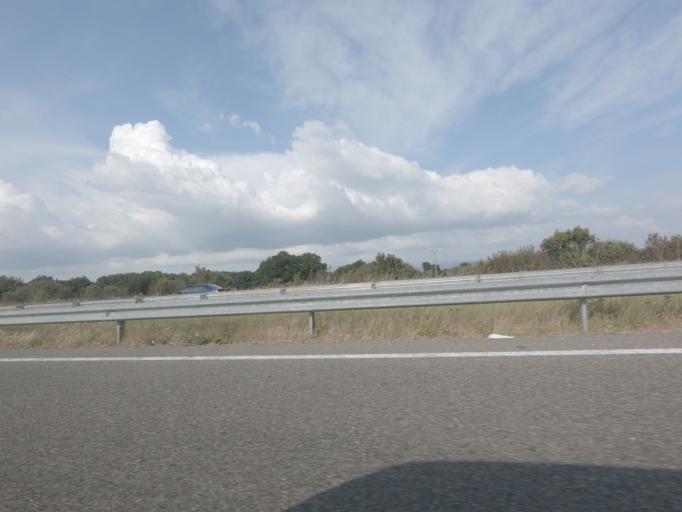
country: ES
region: Galicia
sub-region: Provincia de Ourense
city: Xinzo de Limia
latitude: 42.1241
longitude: -7.7398
